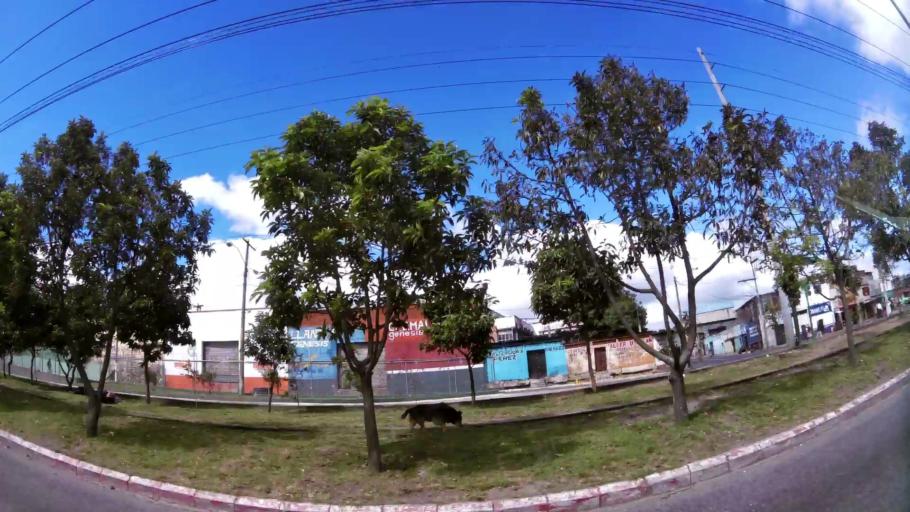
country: GT
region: Guatemala
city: Guatemala City
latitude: 14.6143
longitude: -90.5251
